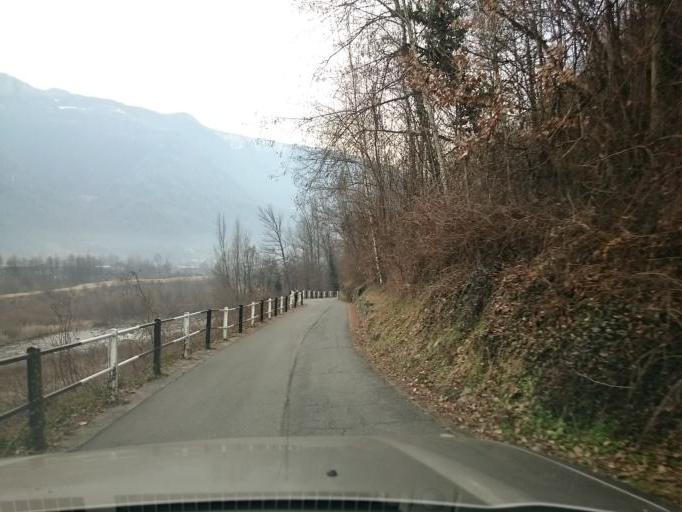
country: IT
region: Lombardy
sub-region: Provincia di Sondrio
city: Vervio
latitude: 46.2466
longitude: 10.2355
